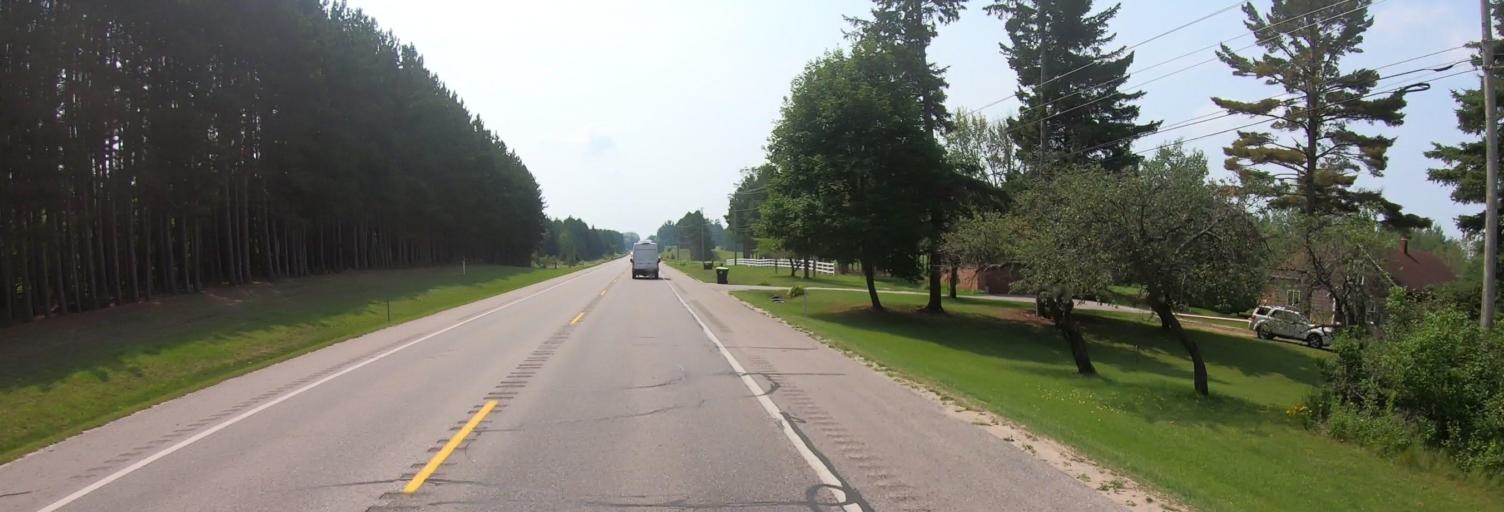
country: US
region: Michigan
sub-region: Luce County
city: Newberry
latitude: 46.3122
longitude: -85.5097
